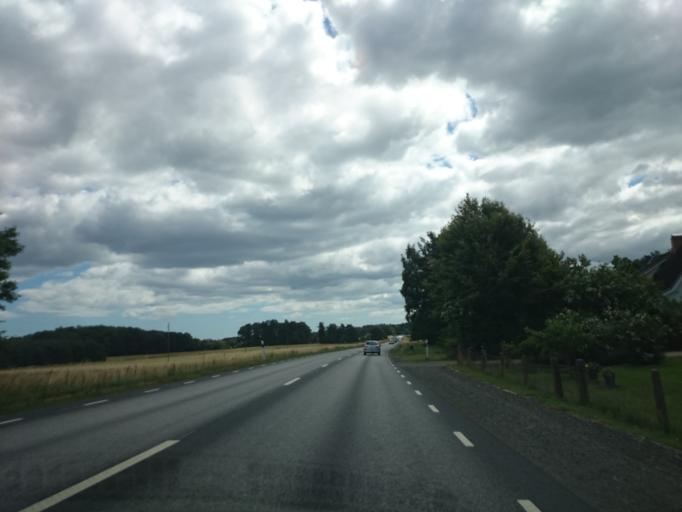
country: SE
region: Skane
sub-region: Kristianstads Kommun
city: Degeberga
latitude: 55.8129
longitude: 14.1360
